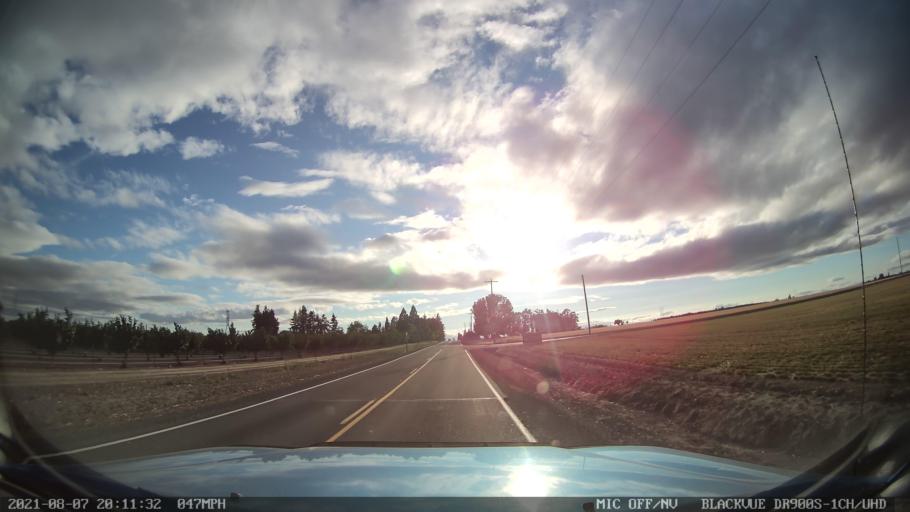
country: US
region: Oregon
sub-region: Marion County
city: Hayesville
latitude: 44.9583
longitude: -122.8923
